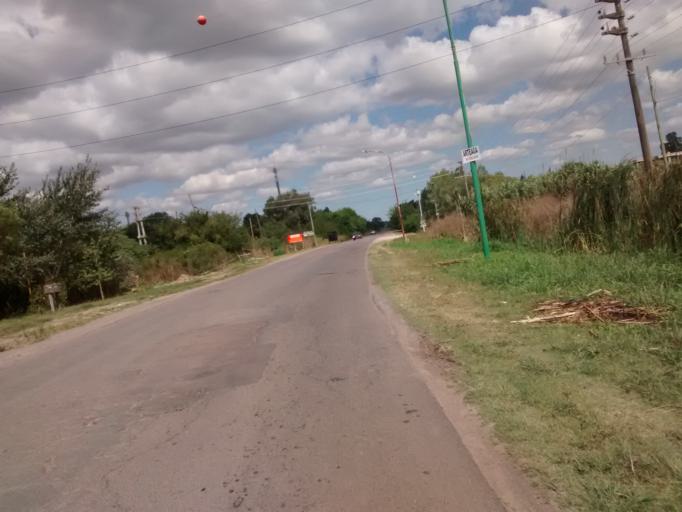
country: AR
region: Buenos Aires
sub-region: Partido de La Plata
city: La Plata
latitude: -34.9721
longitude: -57.9423
